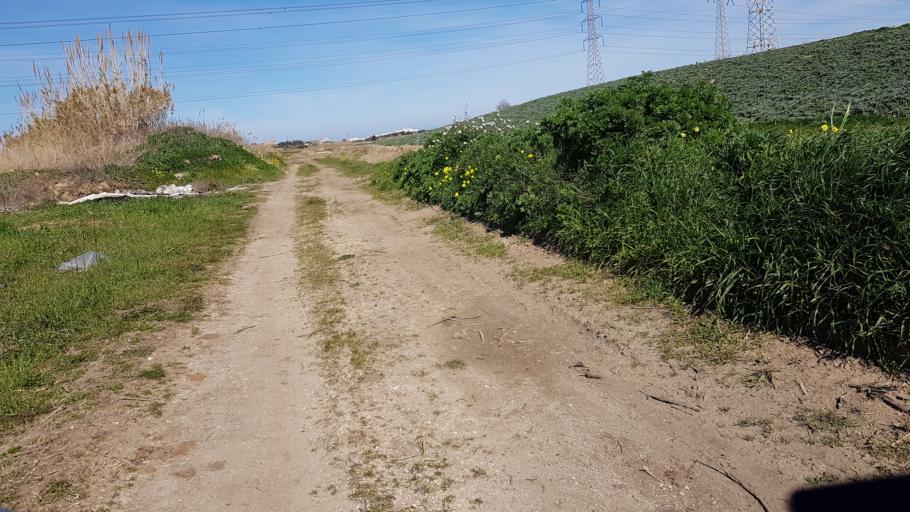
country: IT
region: Apulia
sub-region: Provincia di Brindisi
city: La Rosa
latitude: 40.5974
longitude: 17.9278
